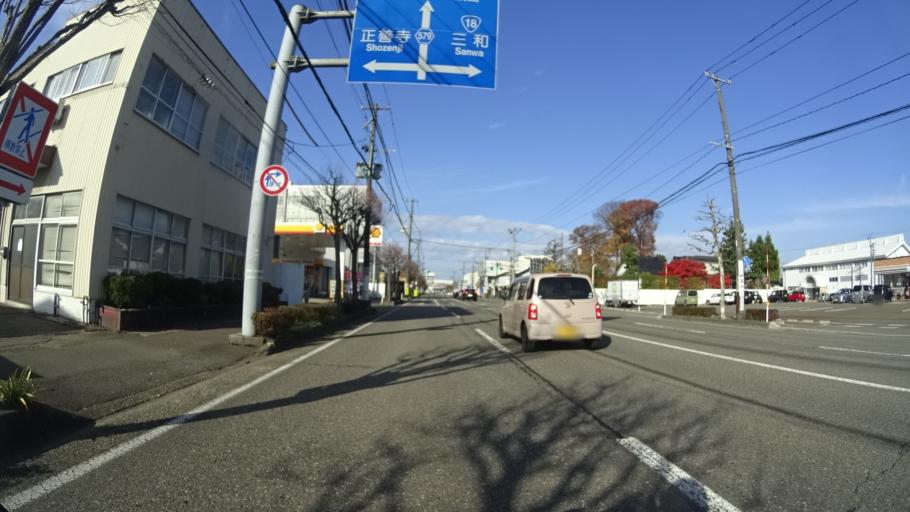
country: JP
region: Niigata
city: Joetsu
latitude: 37.1179
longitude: 138.2519
